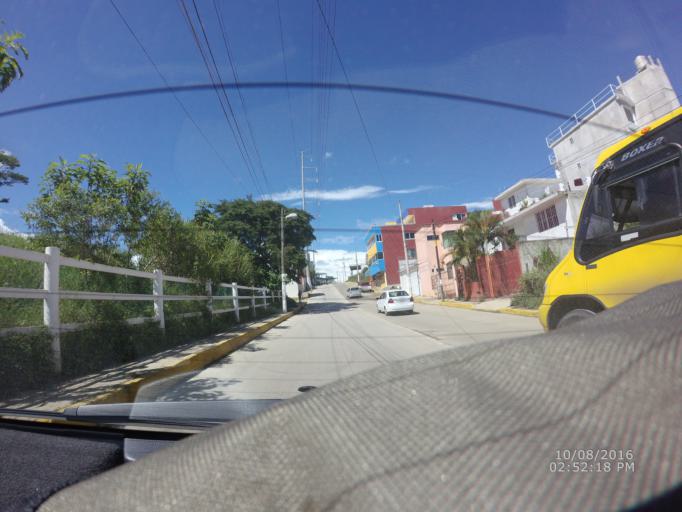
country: MX
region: Veracruz
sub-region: Xalapa
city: Colonia Santa Barbara
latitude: 19.5047
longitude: -96.8788
